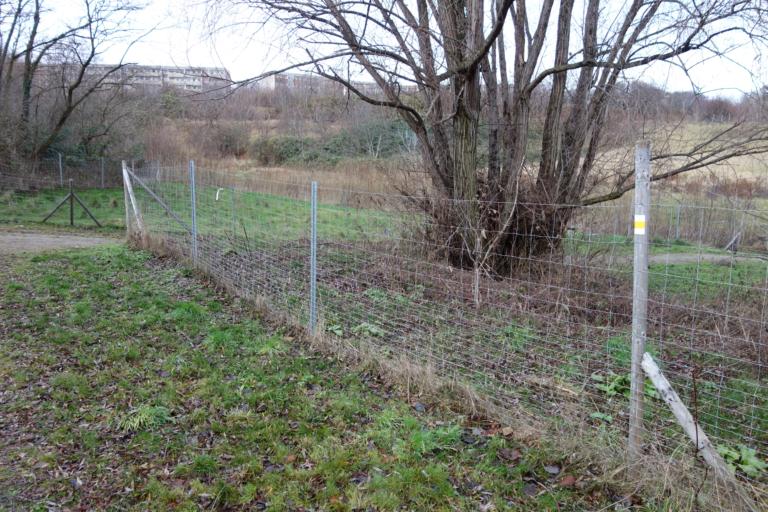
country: DE
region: Saxony
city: Freital
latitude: 51.0503
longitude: 13.6695
